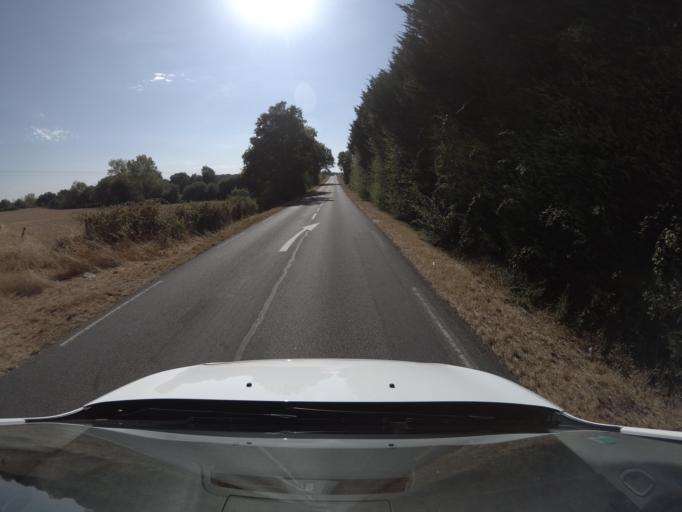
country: FR
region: Poitou-Charentes
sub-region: Departement des Deux-Sevres
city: Argenton-les-Vallees
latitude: 47.0018
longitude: -0.3772
